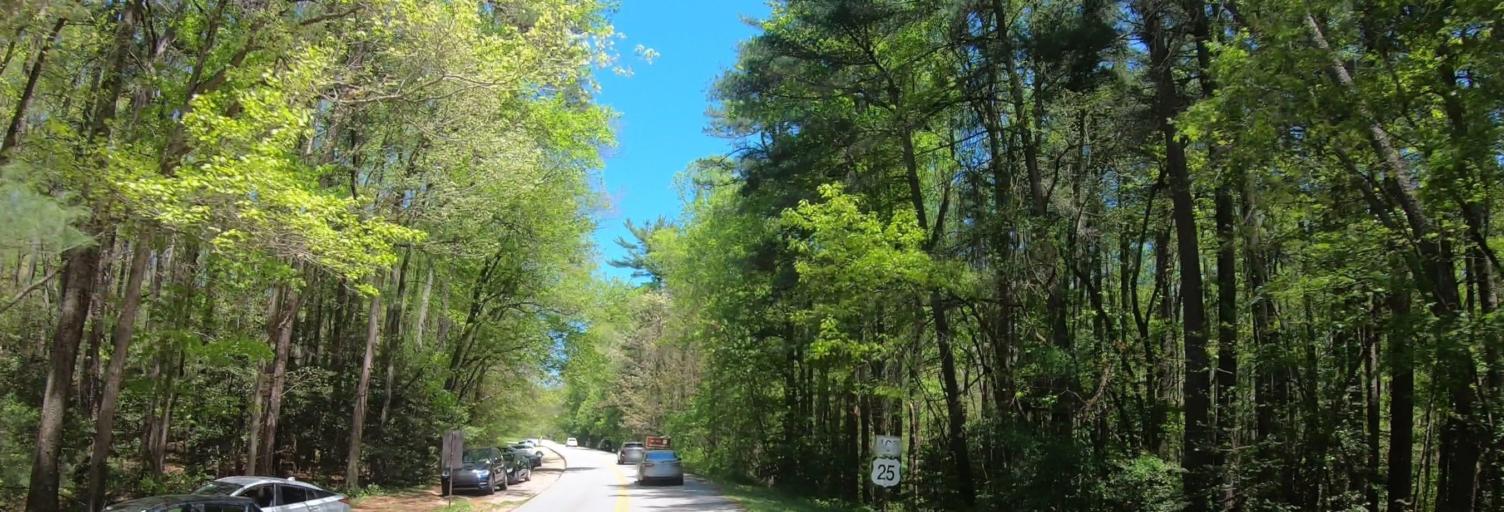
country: US
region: North Carolina
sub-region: Buncombe County
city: Biltmore Forest
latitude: 35.5191
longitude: -82.5316
